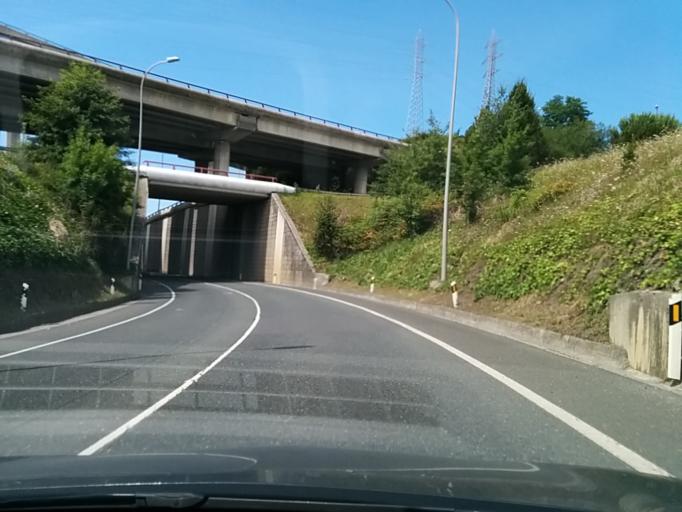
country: ES
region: Basque Country
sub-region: Provincia de Guipuzcoa
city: Lasarte
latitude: 43.2794
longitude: -2.0164
